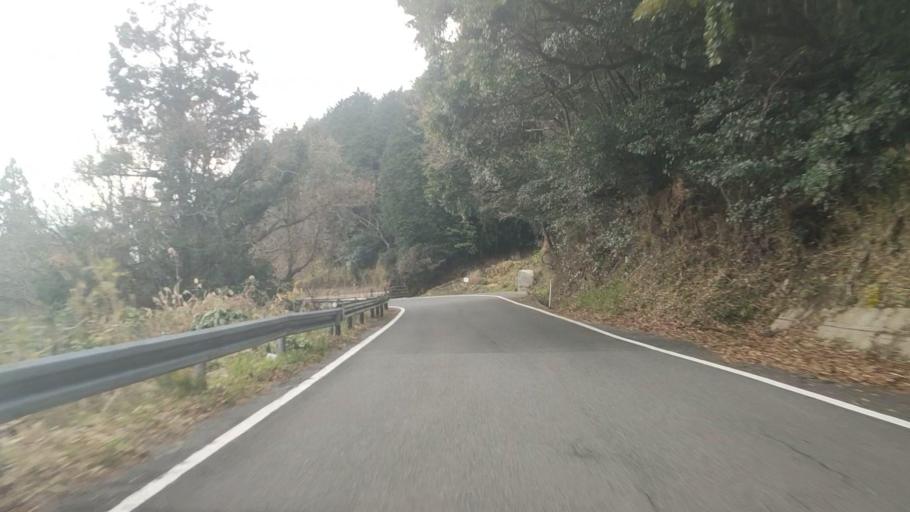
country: JP
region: Nagasaki
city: Shimabara
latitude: 32.7176
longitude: 130.2473
